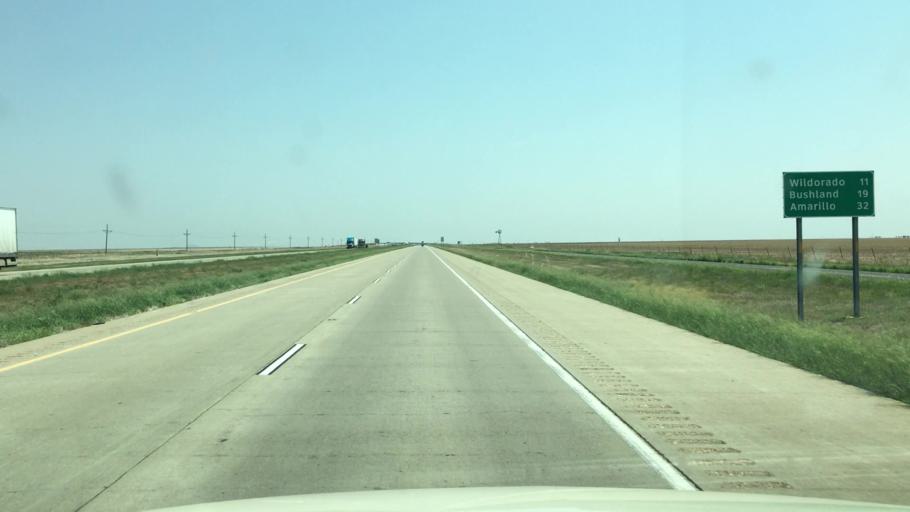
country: US
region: Texas
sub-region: Oldham County
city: Vega
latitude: 35.2368
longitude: -102.3883
